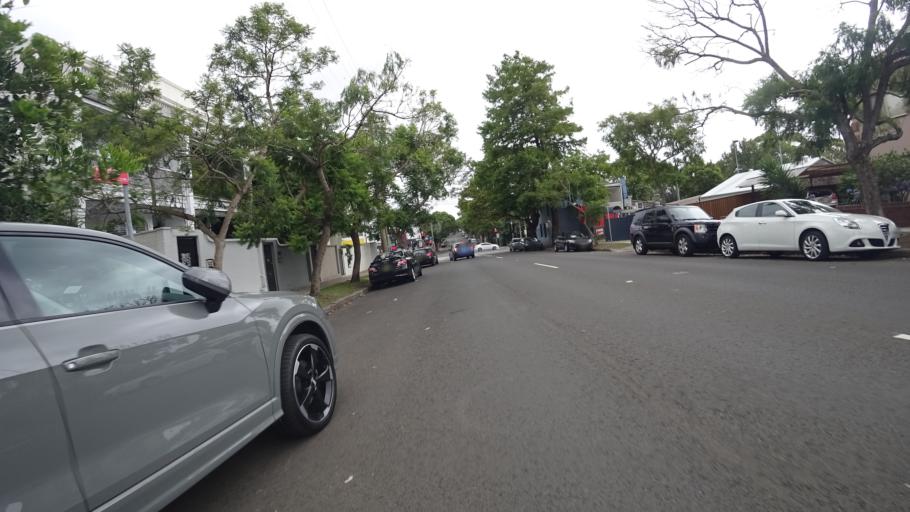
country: AU
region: New South Wales
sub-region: North Sydney
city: Crows Nest
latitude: -33.8292
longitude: 151.2062
